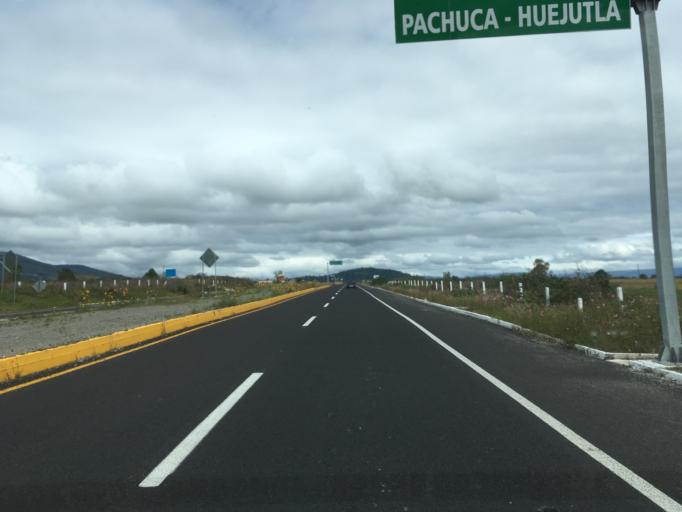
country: MX
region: Hidalgo
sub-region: Atotonilco el Grande
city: Santa Maria Amajac
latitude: 20.3661
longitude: -98.7211
